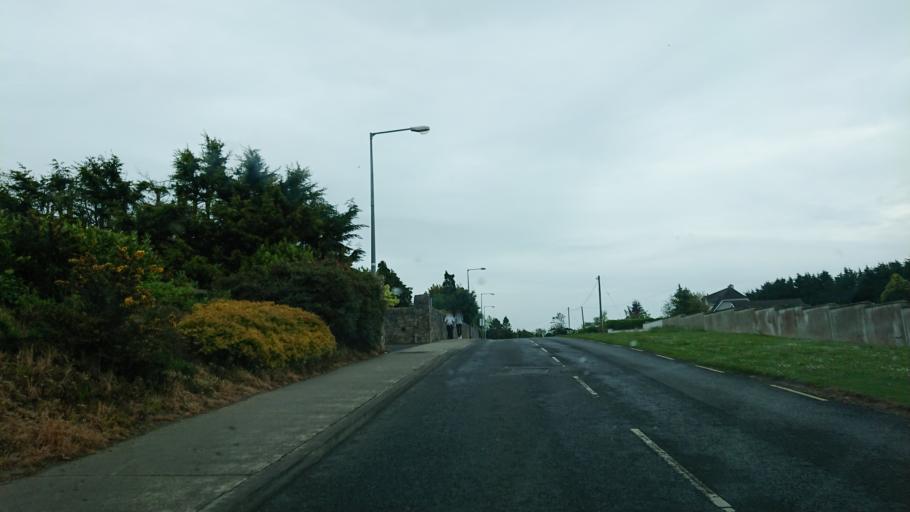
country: IE
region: Munster
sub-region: Waterford
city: Waterford
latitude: 52.2378
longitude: -7.0830
